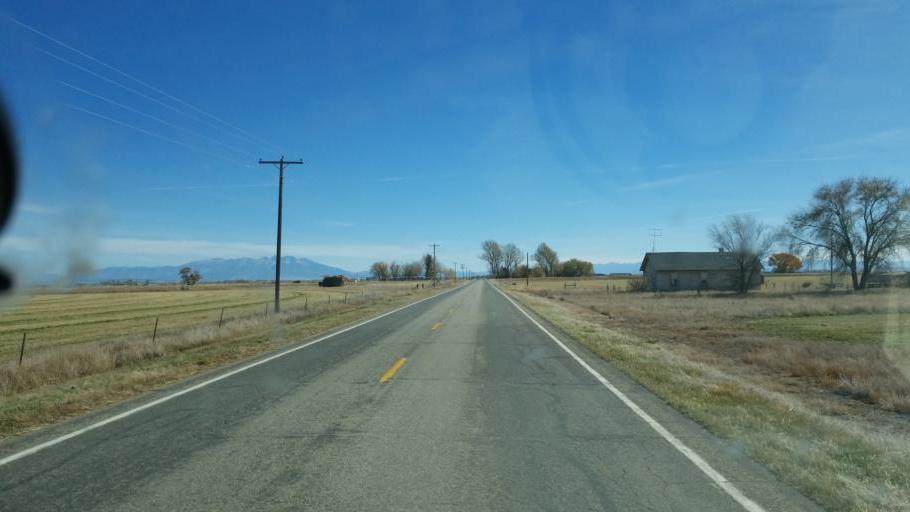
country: US
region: Colorado
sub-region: Rio Grande County
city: Monte Vista
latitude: 37.4300
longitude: -106.1187
